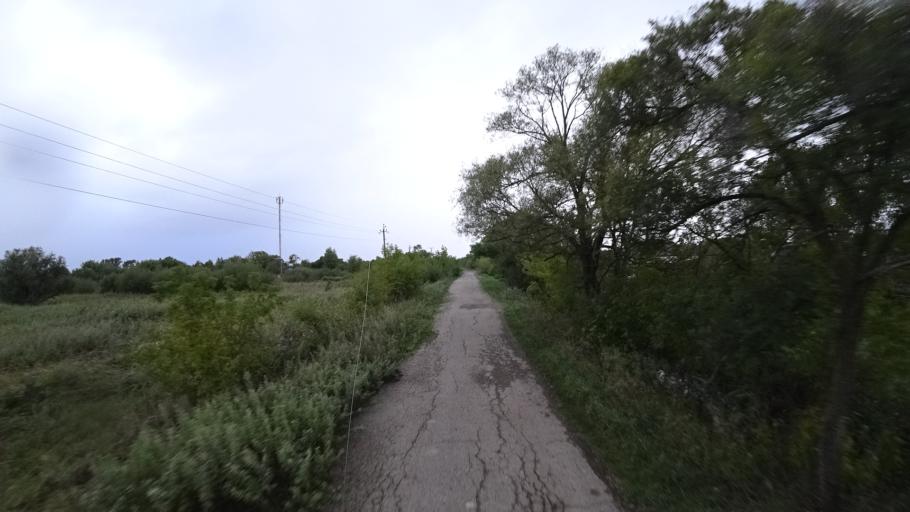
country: RU
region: Primorskiy
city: Chernigovka
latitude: 44.4012
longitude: 132.5315
